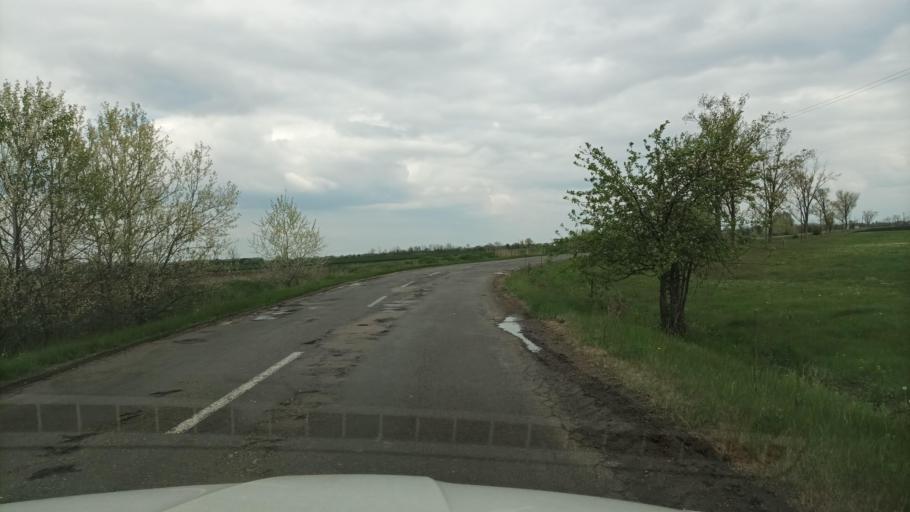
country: HU
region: Pest
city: Abony
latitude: 47.1698
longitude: 19.9784
